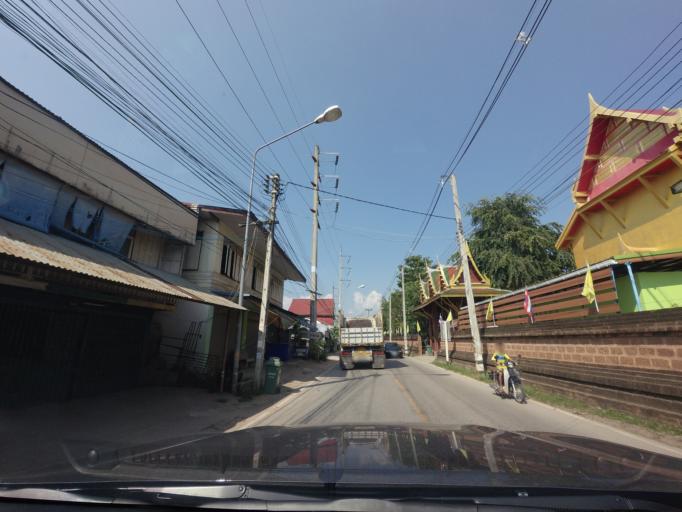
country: TH
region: Phitsanulok
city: Nakhon Thai
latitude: 17.1030
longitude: 100.8385
